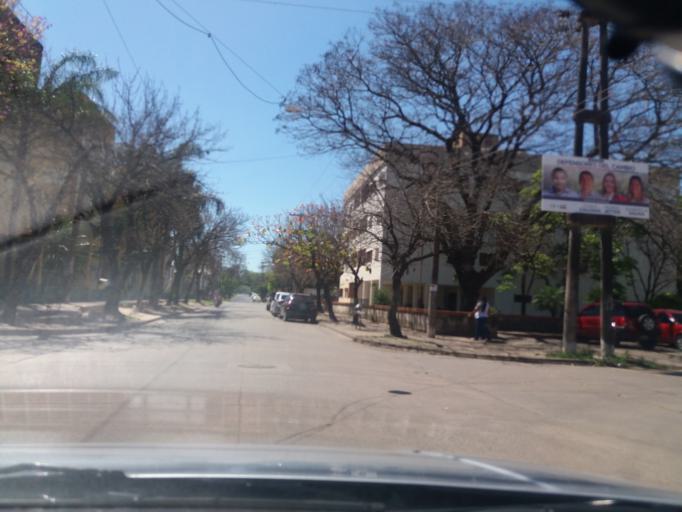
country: AR
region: Corrientes
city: Corrientes
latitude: -27.4855
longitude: -58.8444
